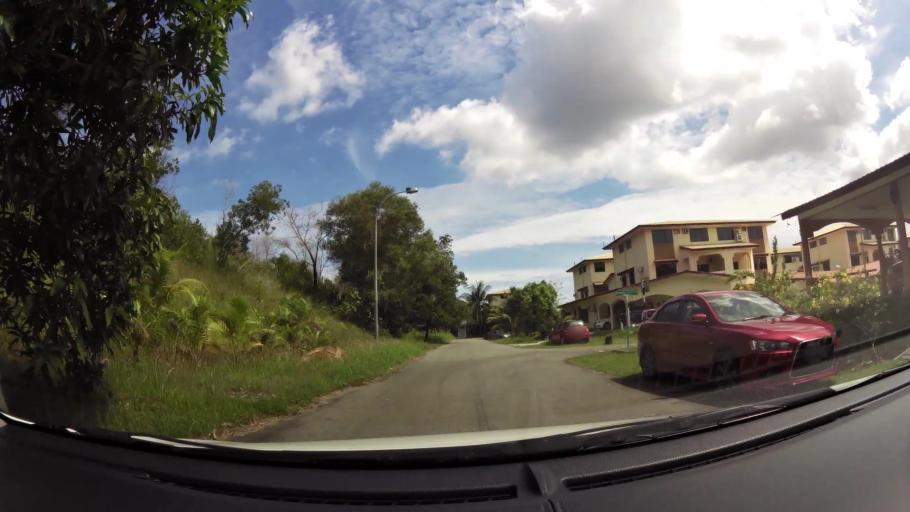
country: BN
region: Brunei and Muara
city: Bandar Seri Begawan
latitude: 4.9299
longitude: 114.8938
